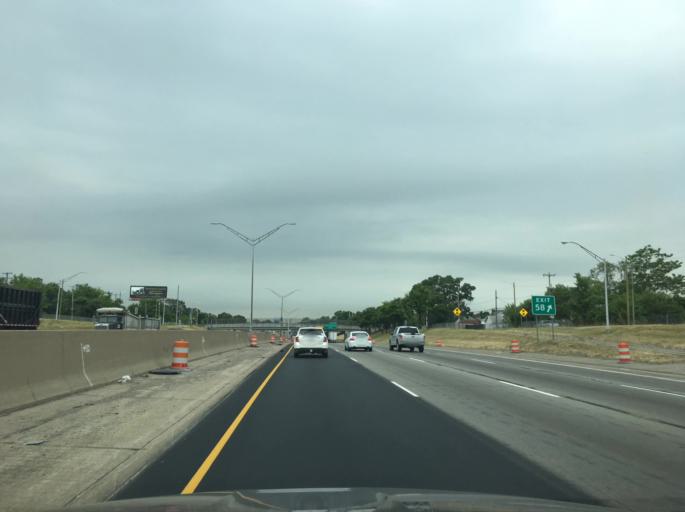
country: US
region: Michigan
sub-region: Oakland County
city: Hazel Park
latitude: 42.4357
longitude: -83.0949
